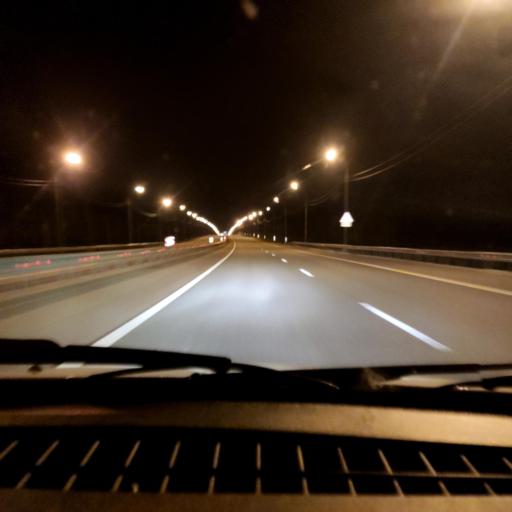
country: RU
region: Lipetsk
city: Zadonsk
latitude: 52.3307
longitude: 39.0118
